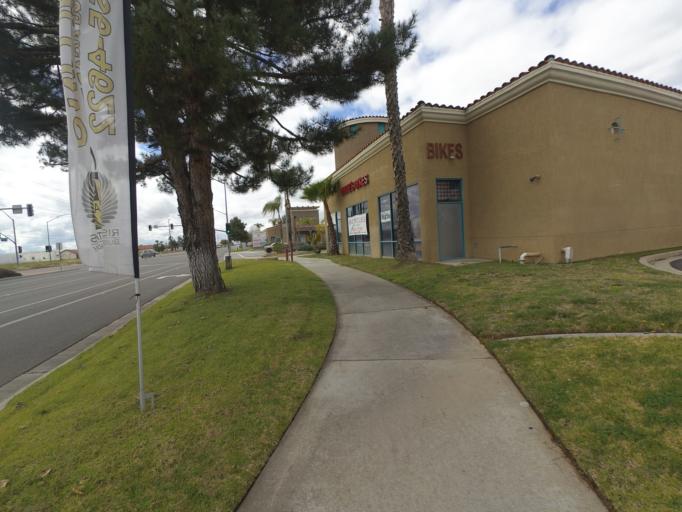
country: US
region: California
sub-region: Riverside County
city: Moreno Valley
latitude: 33.9174
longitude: -117.2473
